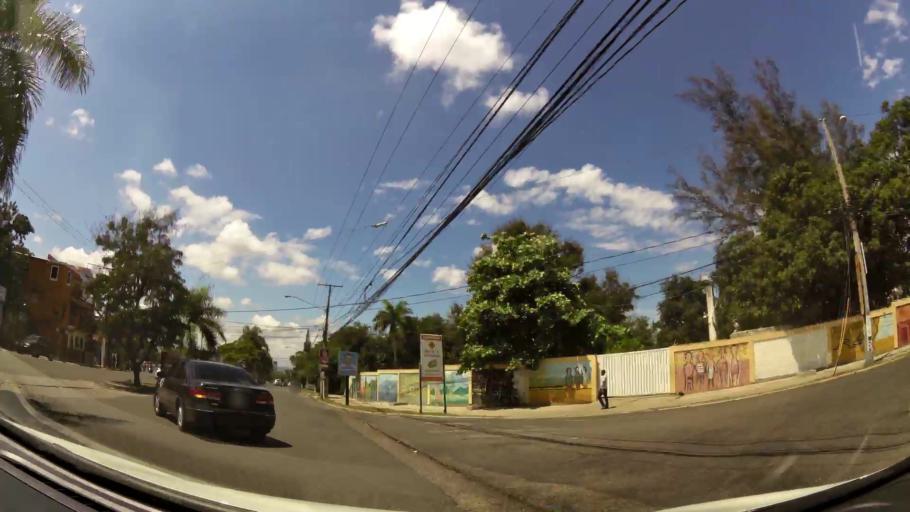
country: DO
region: Santiago
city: Santiago de los Caballeros
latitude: 19.4625
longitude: -70.6771
